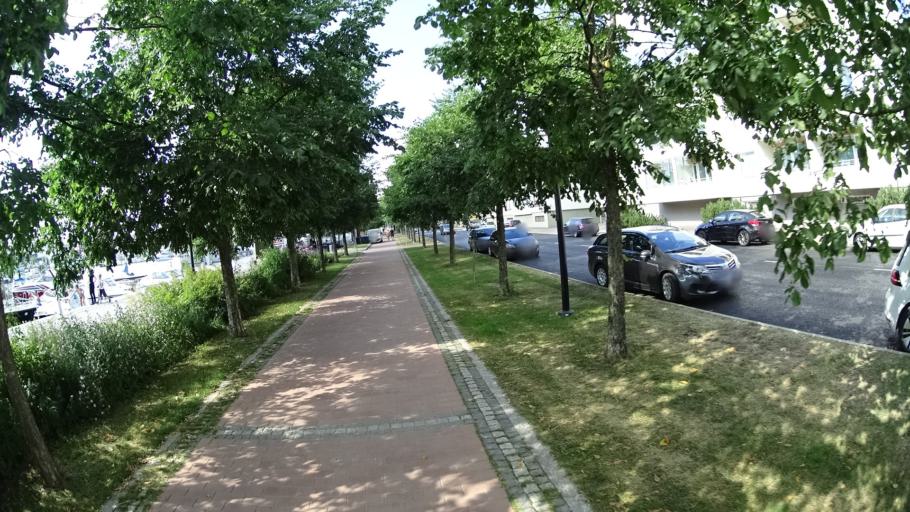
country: FI
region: Uusimaa
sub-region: Porvoo
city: Porvoo
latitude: 60.3883
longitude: 25.6635
